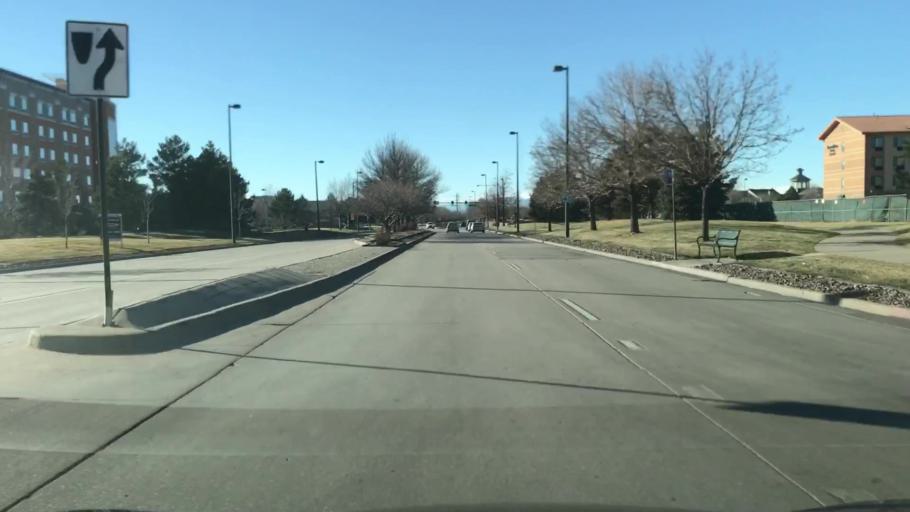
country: US
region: Colorado
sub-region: Adams County
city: Aurora
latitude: 39.7729
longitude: -104.7992
